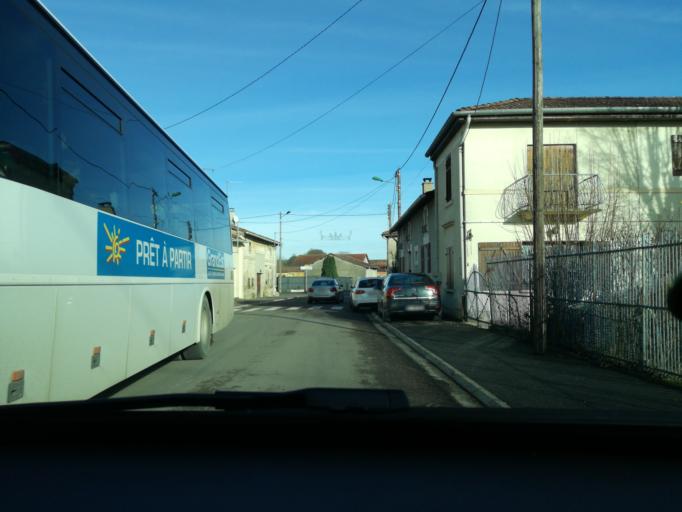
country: FR
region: Lorraine
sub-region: Departement de la Meuse
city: Revigny-sur-Ornain
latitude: 48.8236
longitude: 5.0440
